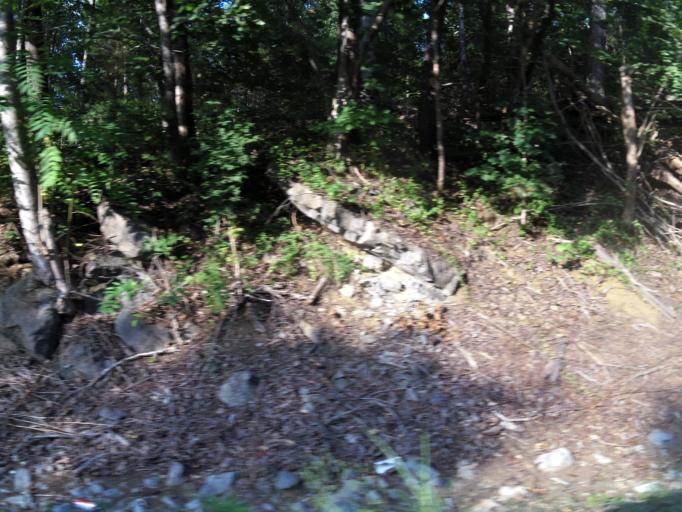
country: US
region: Tennessee
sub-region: Union County
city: Condon
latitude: 36.1887
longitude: -83.8159
